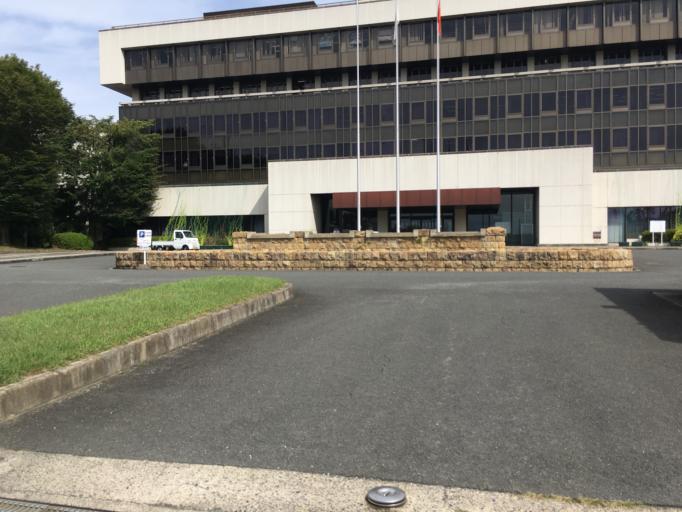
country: JP
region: Nara
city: Nara-shi
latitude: 34.6845
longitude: 135.8049
